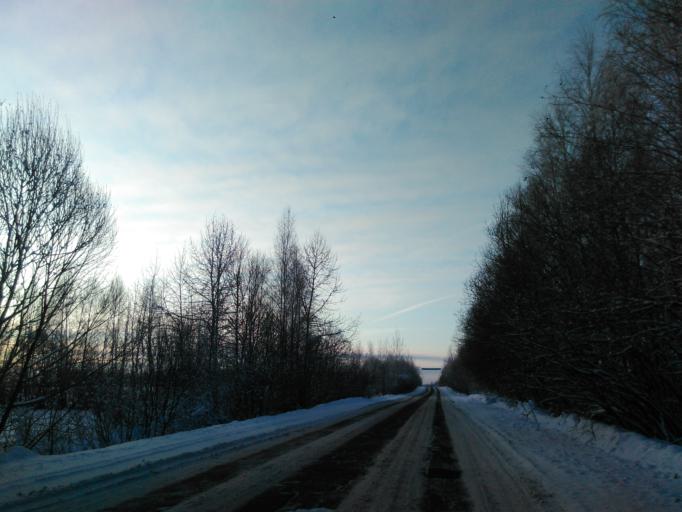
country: RU
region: Tverskaya
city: Zavidovo
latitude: 56.6265
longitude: 36.6156
